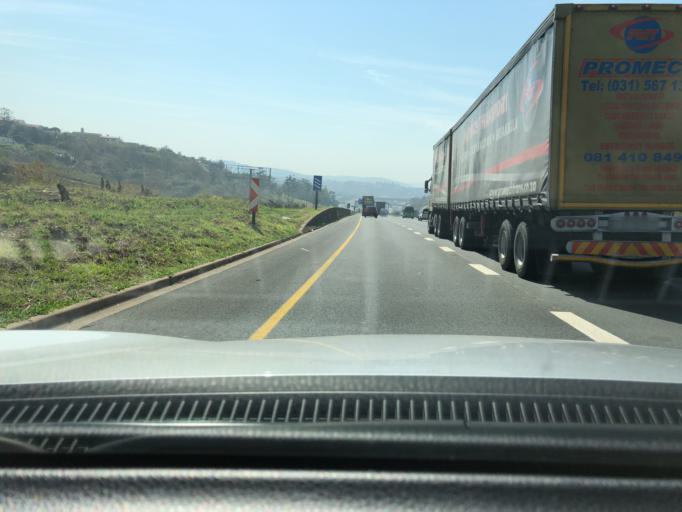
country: ZA
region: KwaZulu-Natal
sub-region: eThekwini Metropolitan Municipality
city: Berea
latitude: -29.8161
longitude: 30.9728
